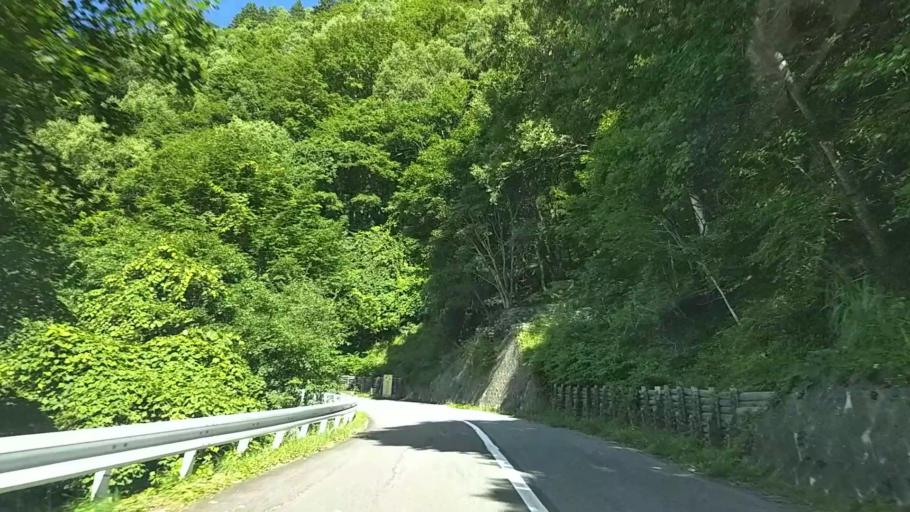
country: JP
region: Nagano
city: Matsumoto
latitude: 36.1958
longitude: 138.1175
